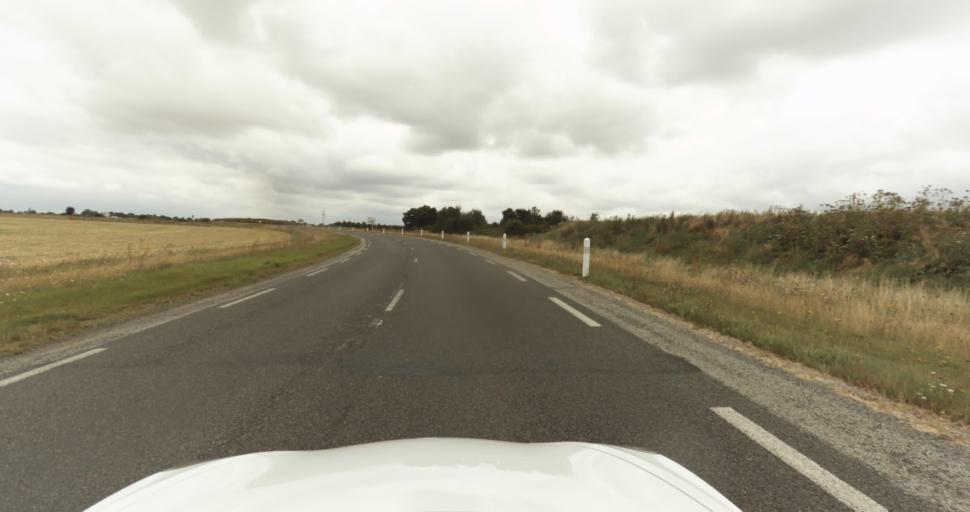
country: FR
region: Haute-Normandie
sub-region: Departement de l'Eure
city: Saint-Sebastien-de-Morsent
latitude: 49.0343
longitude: 1.0883
